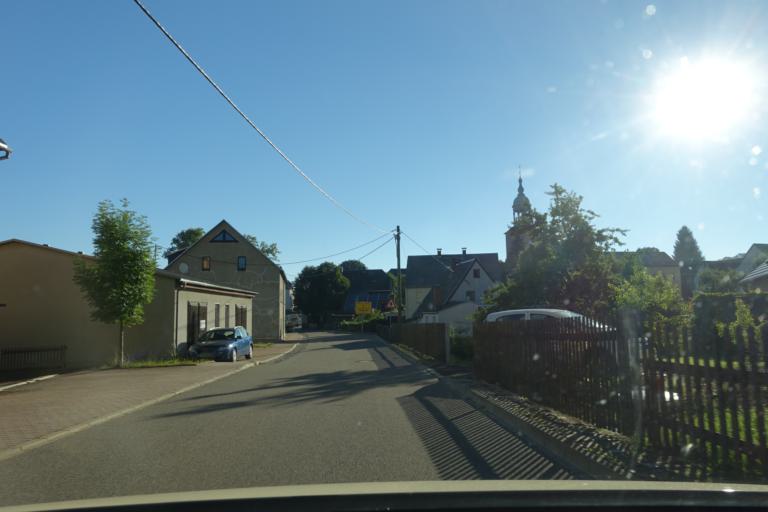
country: DE
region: Saxony
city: Eppendorf
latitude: 50.7835
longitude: 13.2678
